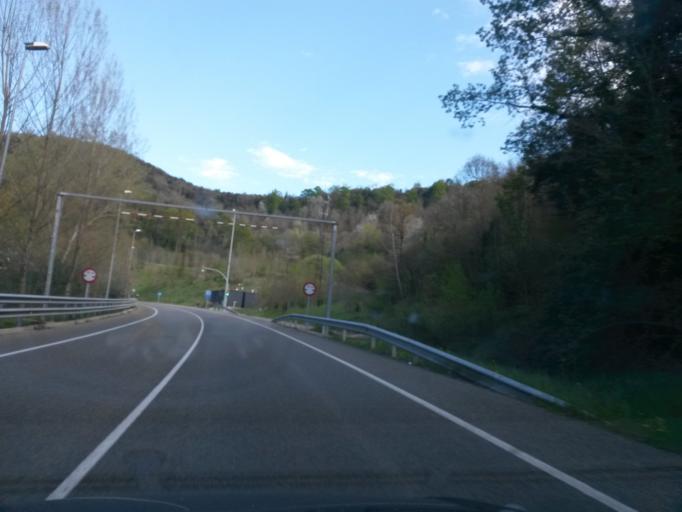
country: ES
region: Catalonia
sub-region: Provincia de Girona
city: Bas
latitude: 42.1253
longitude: 2.4537
